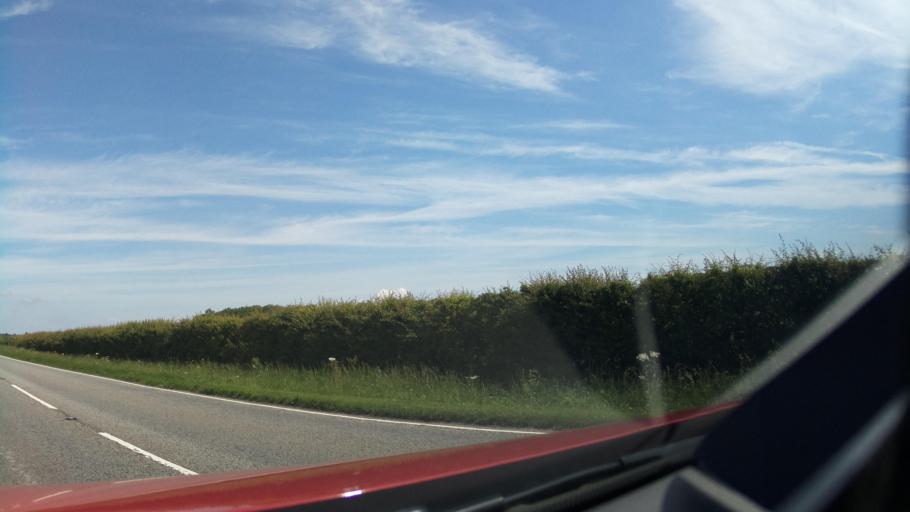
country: GB
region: England
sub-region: Lincolnshire
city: Burton
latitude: 53.3692
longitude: -0.5459
